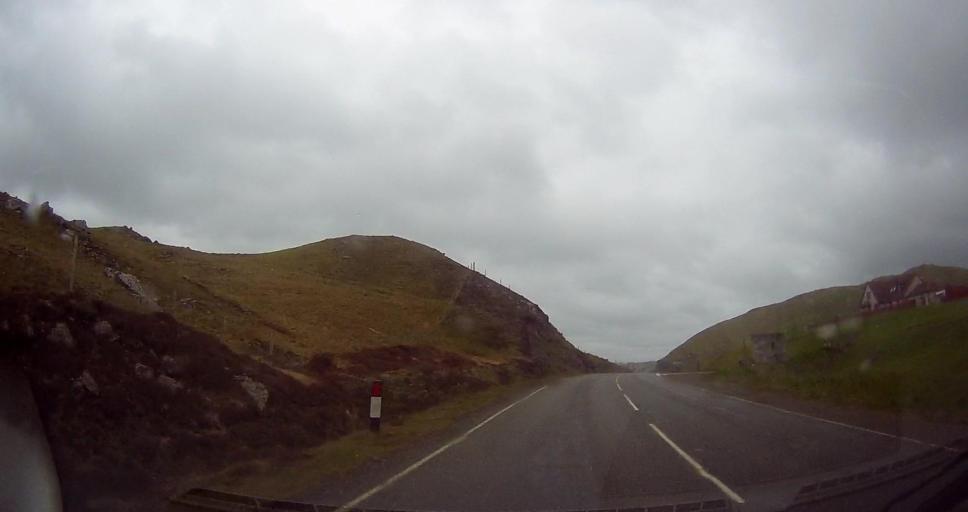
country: GB
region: Scotland
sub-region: Shetland Islands
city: Lerwick
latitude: 60.4060
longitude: -1.3868
